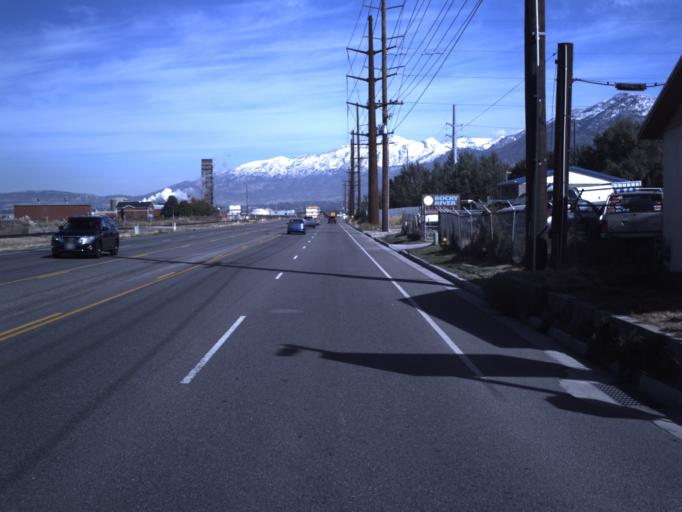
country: US
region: Utah
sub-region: Utah County
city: Lindon
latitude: 40.3146
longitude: -111.7351
